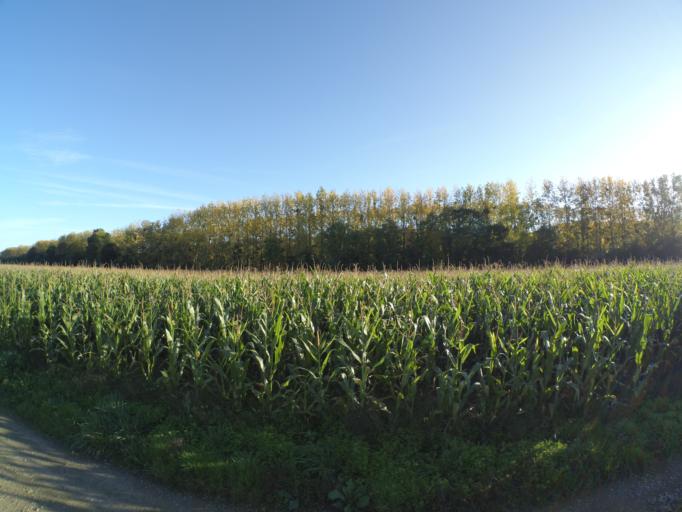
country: FR
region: Brittany
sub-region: Departement du Morbihan
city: Peillac
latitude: 47.7233
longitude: -2.1813
